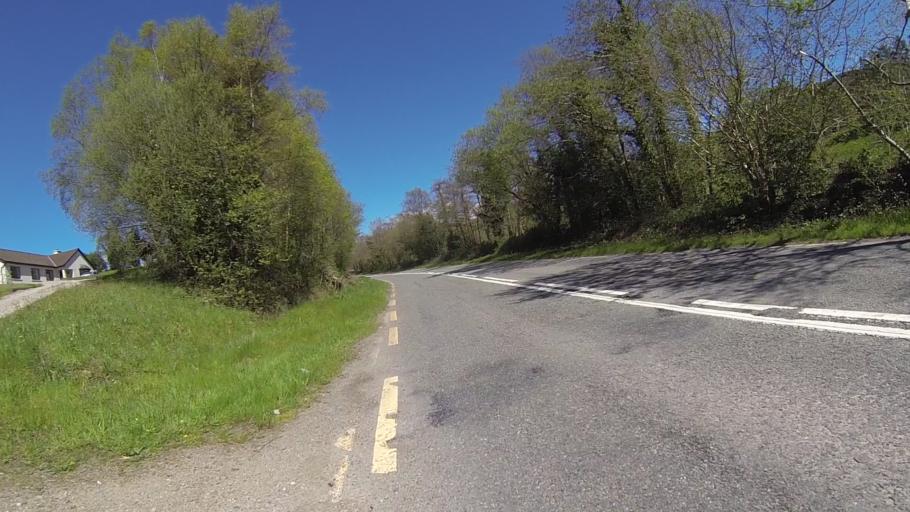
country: IE
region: Munster
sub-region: Ciarrai
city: Kenmare
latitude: 51.8993
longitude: -9.5992
